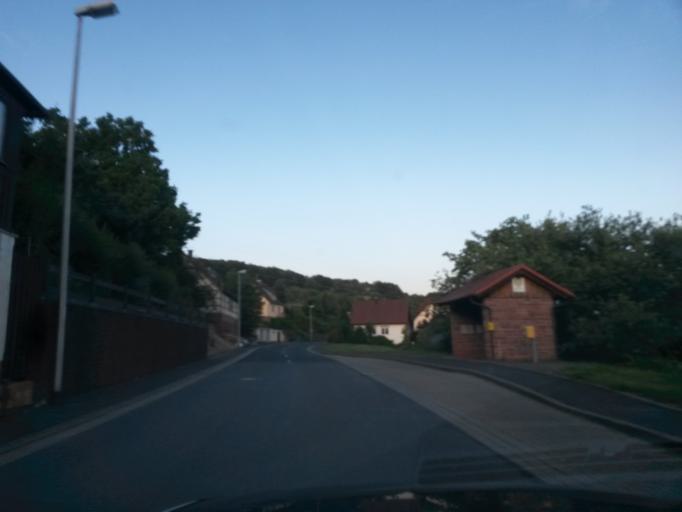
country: DE
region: Bavaria
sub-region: Regierungsbezirk Unterfranken
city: Rothenfels
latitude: 49.8816
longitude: 9.5822
